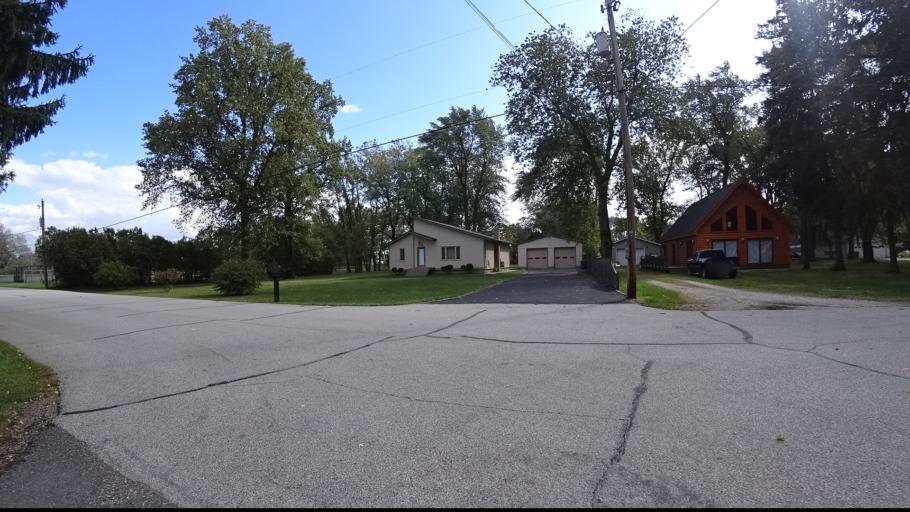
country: US
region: Indiana
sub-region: Porter County
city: Burns Harbor
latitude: 41.6104
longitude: -87.1156
